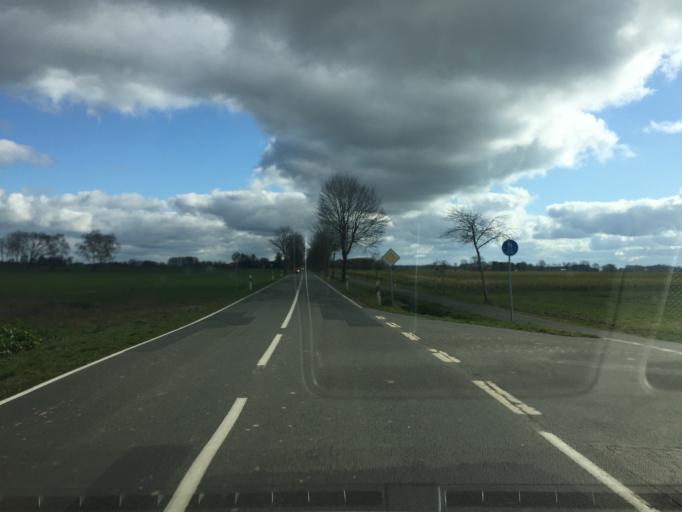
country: DE
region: Lower Saxony
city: Engeln
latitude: 52.7977
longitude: 8.9199
